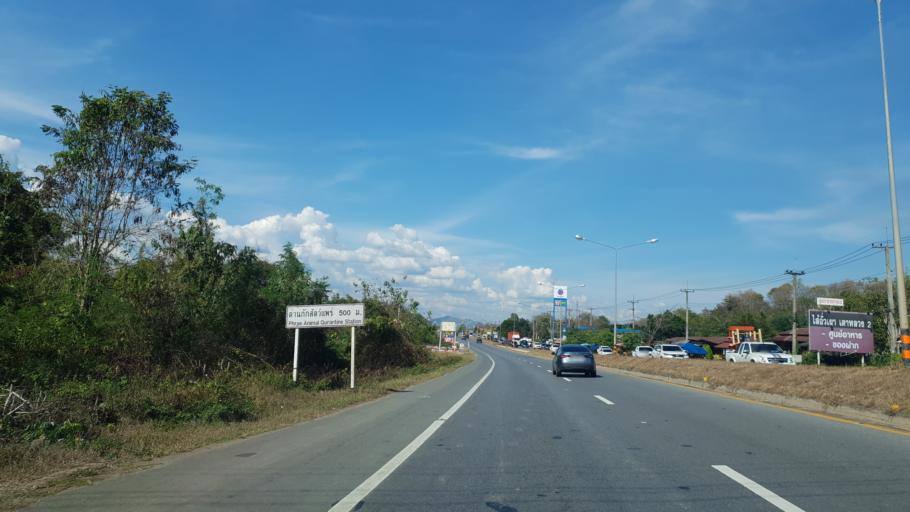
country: TH
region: Phrae
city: Den Chai
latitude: 17.9539
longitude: 100.0683
